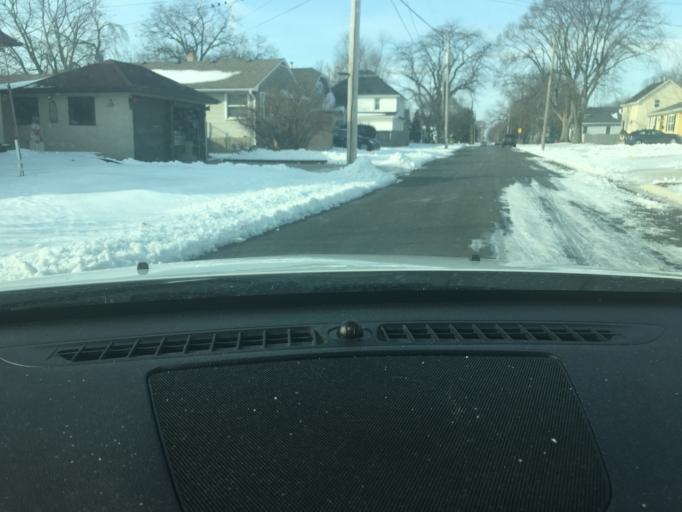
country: US
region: Illinois
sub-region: LaSalle County
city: Peru
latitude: 41.3331
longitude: -89.1254
